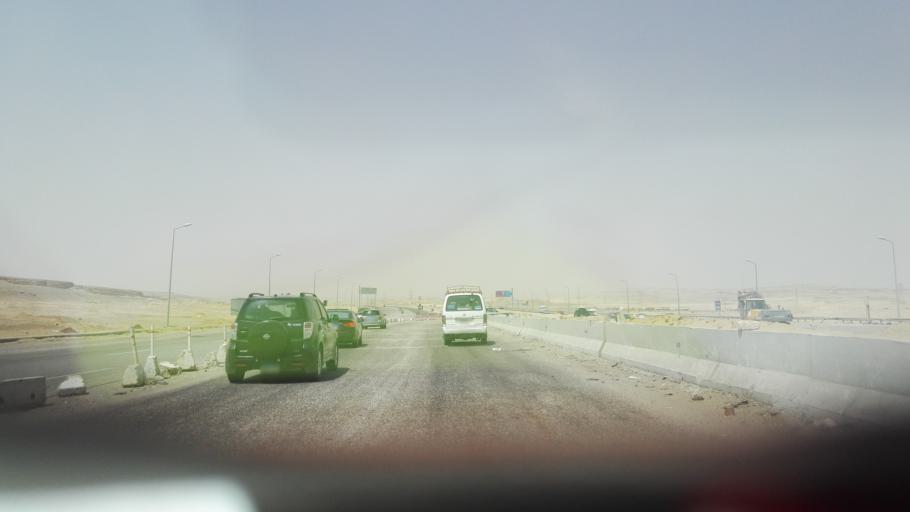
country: EG
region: As Suways
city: Ain Sukhna
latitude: 29.7593
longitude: 32.0111
